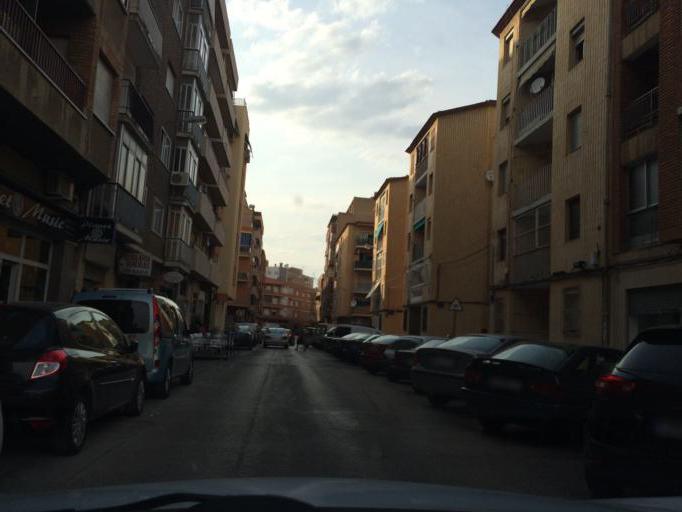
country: ES
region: Castille-La Mancha
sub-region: Provincia de Albacete
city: Albacete
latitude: 38.9876
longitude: -1.8645
